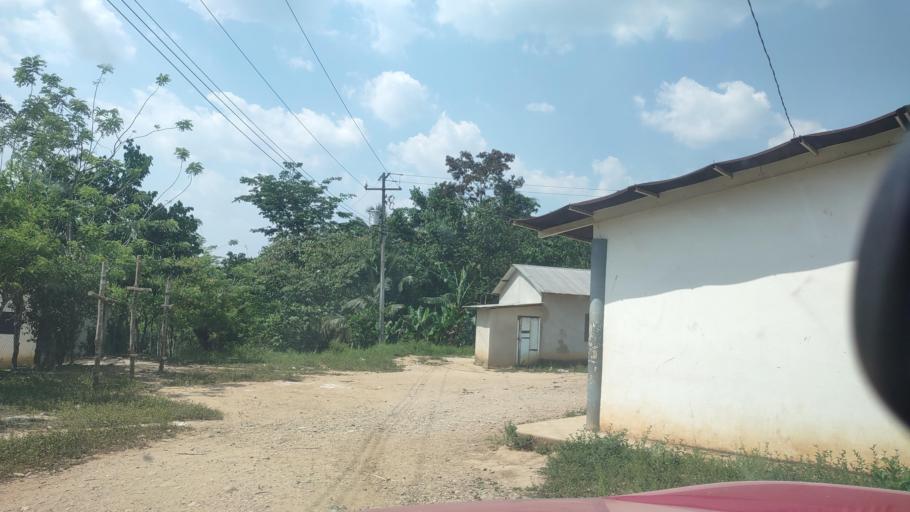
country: MX
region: Chiapas
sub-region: Tecpatan
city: Raudales Malpaso
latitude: 17.3456
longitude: -93.7583
